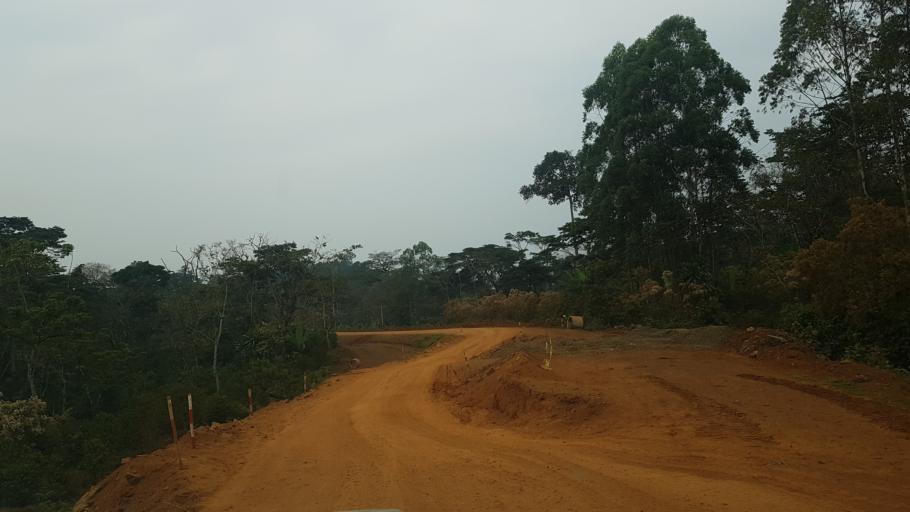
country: ET
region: Oromiya
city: Gore
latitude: 7.8917
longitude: 35.4876
